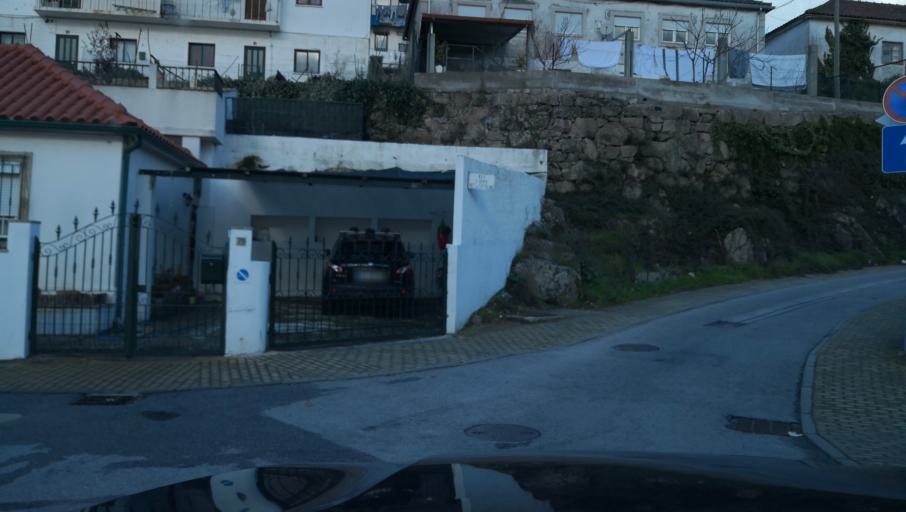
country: PT
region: Vila Real
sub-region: Vila Real
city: Vila Real
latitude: 41.3126
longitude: -7.7260
